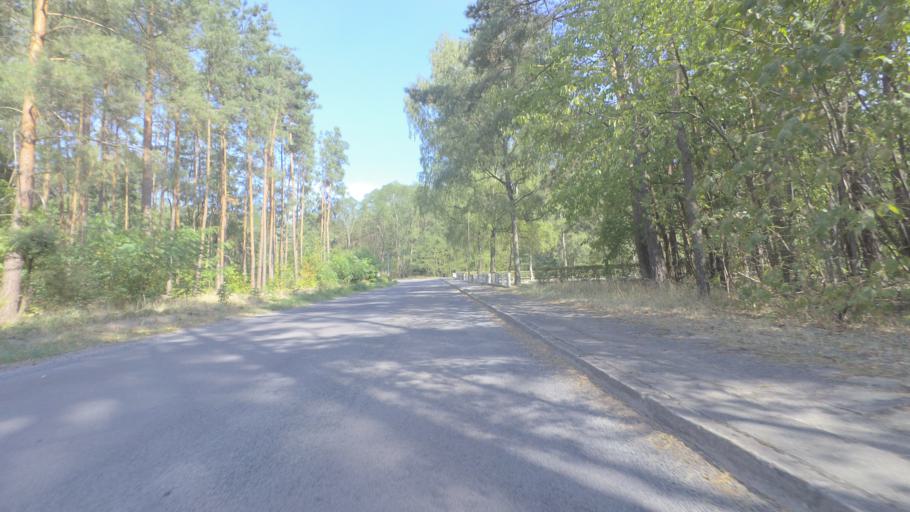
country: DE
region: Brandenburg
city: Am Mellensee
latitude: 52.1916
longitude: 13.3667
